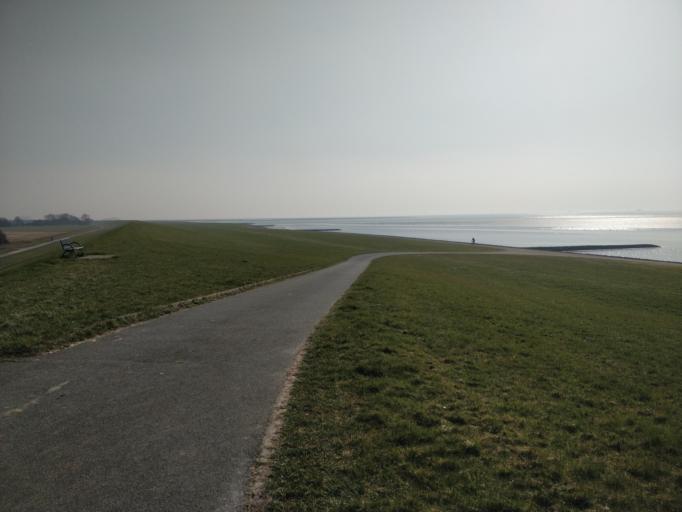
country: DE
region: Lower Saxony
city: Misselwarden
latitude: 53.6838
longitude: 8.4847
